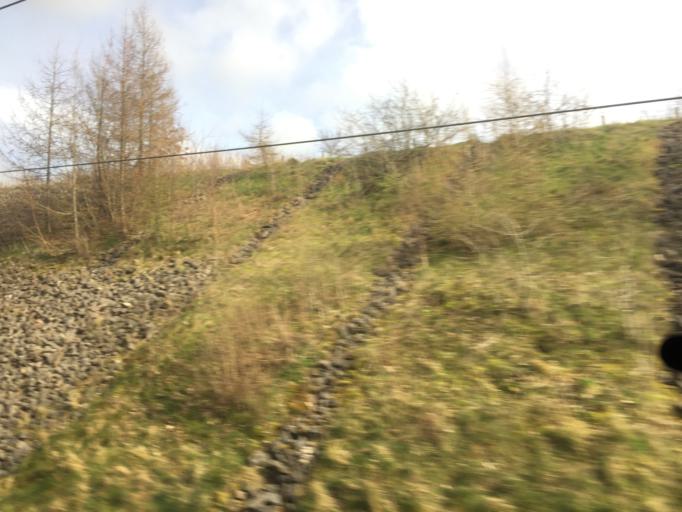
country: GB
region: England
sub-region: Cumbria
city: Penrith
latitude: 54.7448
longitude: -2.8086
